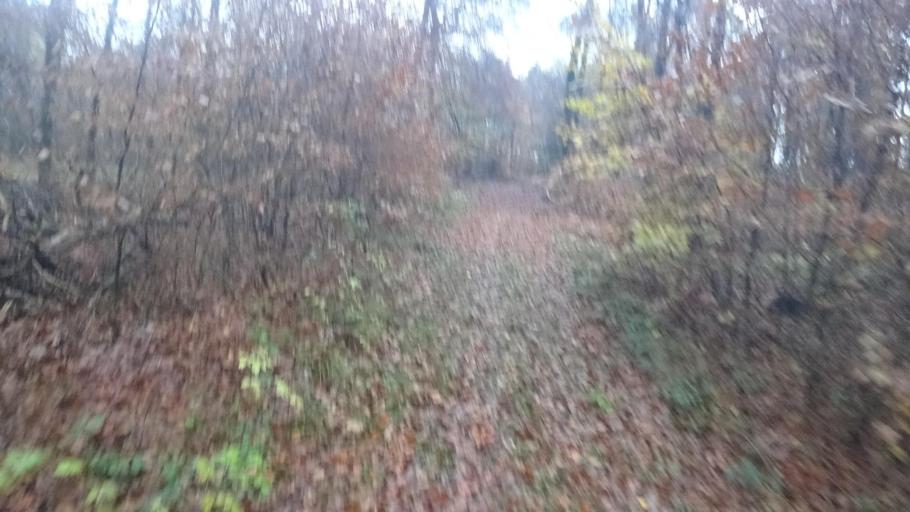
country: DE
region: Rheinland-Pfalz
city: Wiebelsheim
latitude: 50.0757
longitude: 7.6505
